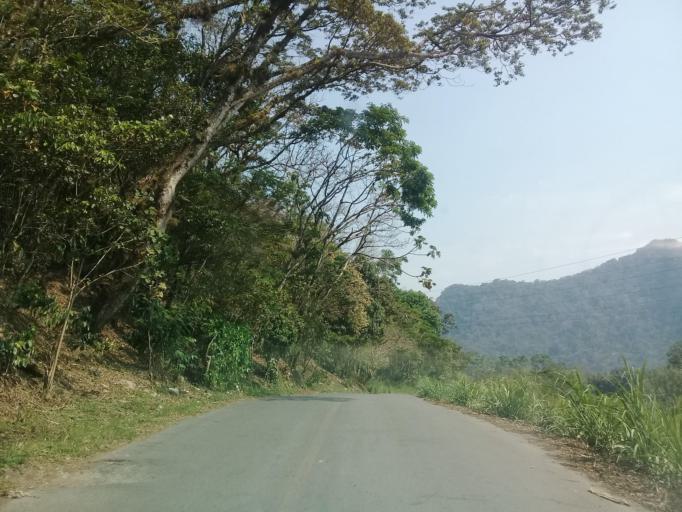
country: MX
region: Veracruz
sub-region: Ixtaczoquitlan
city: Campo Chico
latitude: 18.8302
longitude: -97.0120
